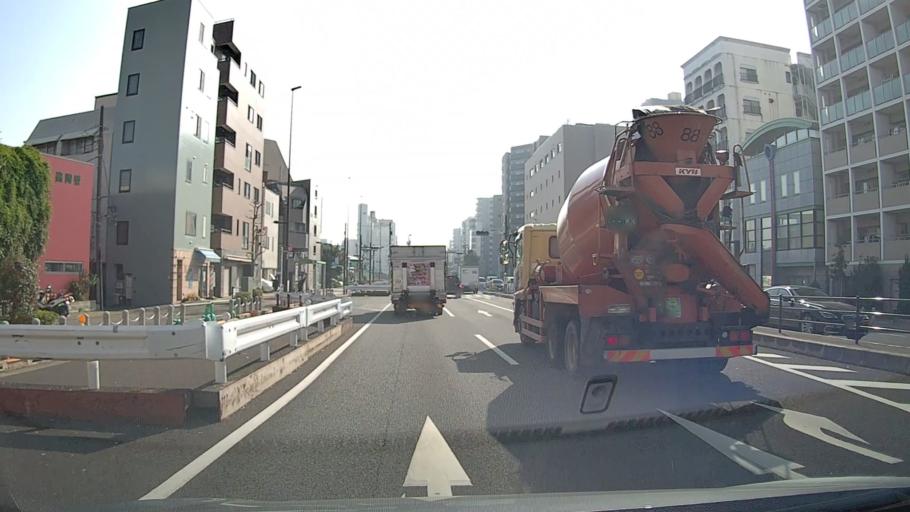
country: JP
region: Tokyo
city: Tokyo
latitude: 35.7391
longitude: 139.7329
